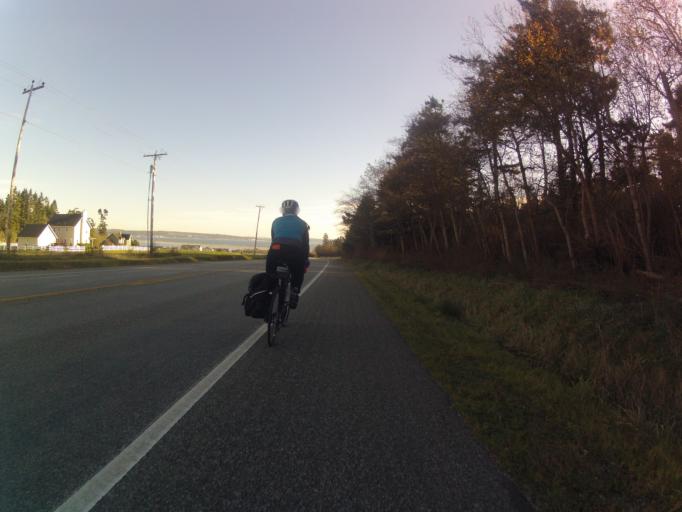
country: US
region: Washington
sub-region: Island County
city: Coupeville
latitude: 48.1752
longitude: -122.6835
